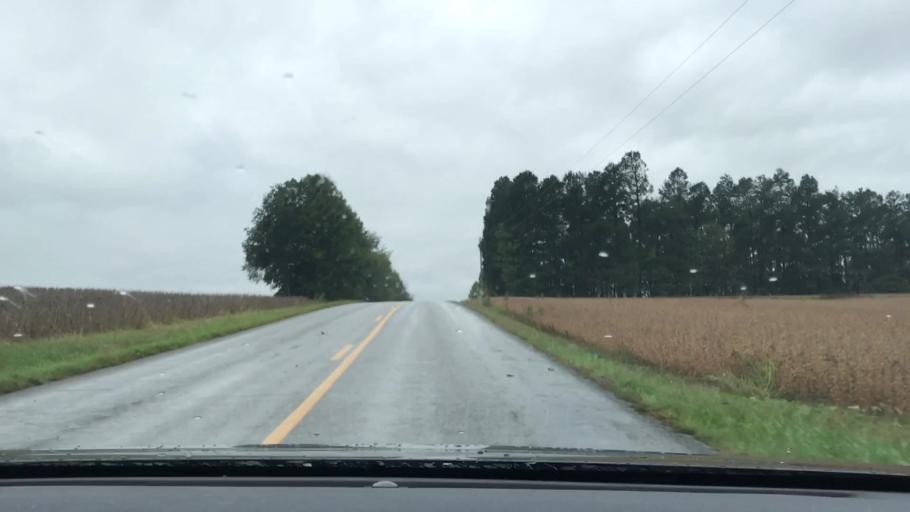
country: US
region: Kentucky
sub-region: McLean County
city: Calhoun
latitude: 37.3994
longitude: -87.2733
